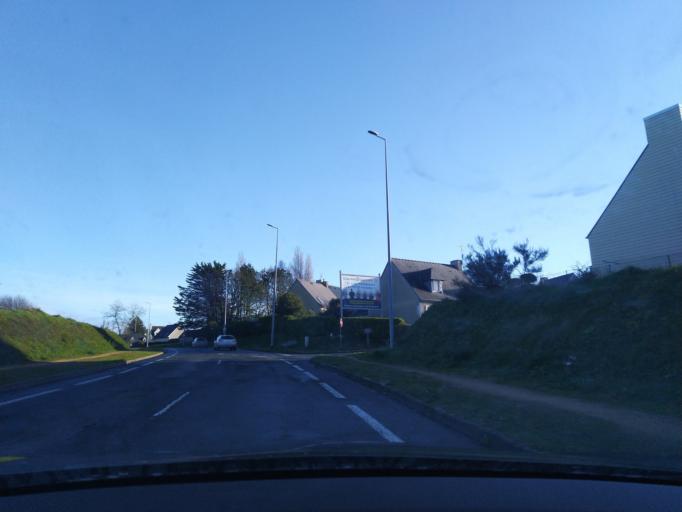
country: FR
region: Brittany
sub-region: Departement du Finistere
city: Morlaix
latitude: 48.5888
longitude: -3.8266
